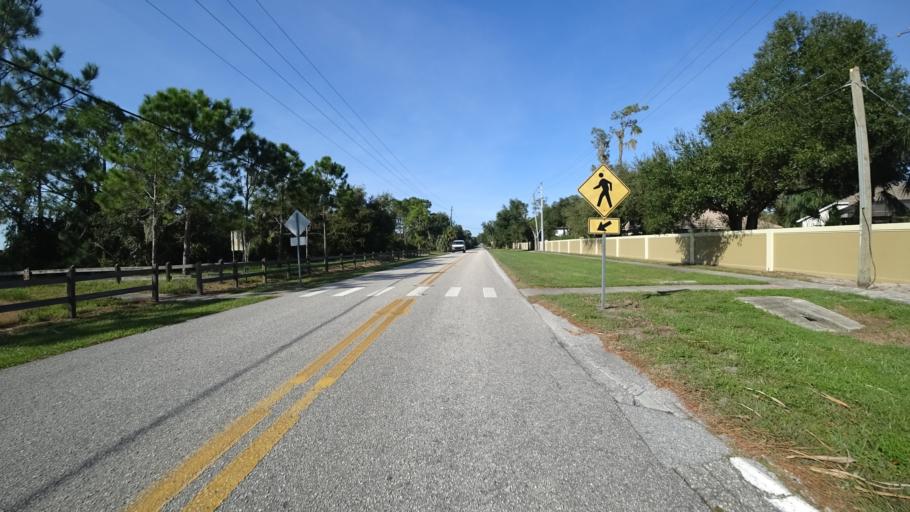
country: US
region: Florida
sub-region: Sarasota County
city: Desoto Lakes
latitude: 27.4327
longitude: -82.4810
